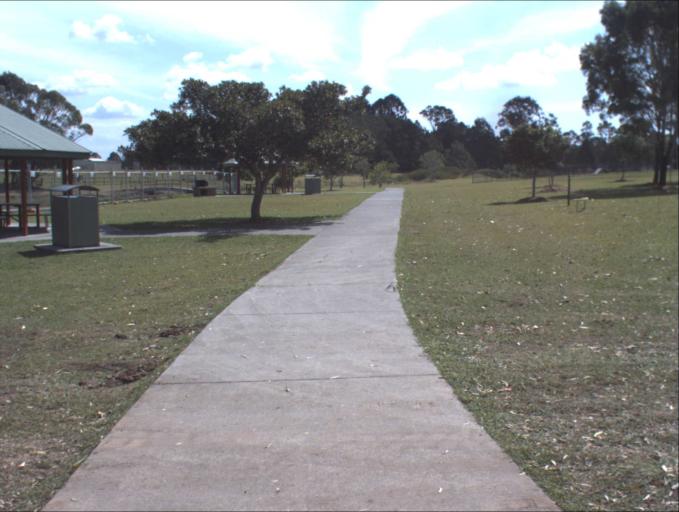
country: AU
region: Queensland
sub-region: Logan
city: Slacks Creek
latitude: -27.6741
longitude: 153.1536
